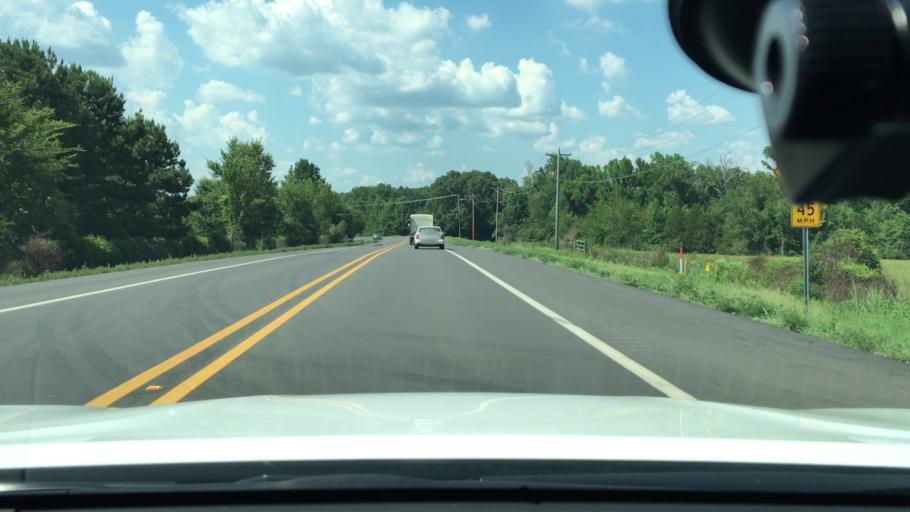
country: US
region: Arkansas
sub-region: Johnson County
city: Clarksville
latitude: 35.4487
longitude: -93.5292
